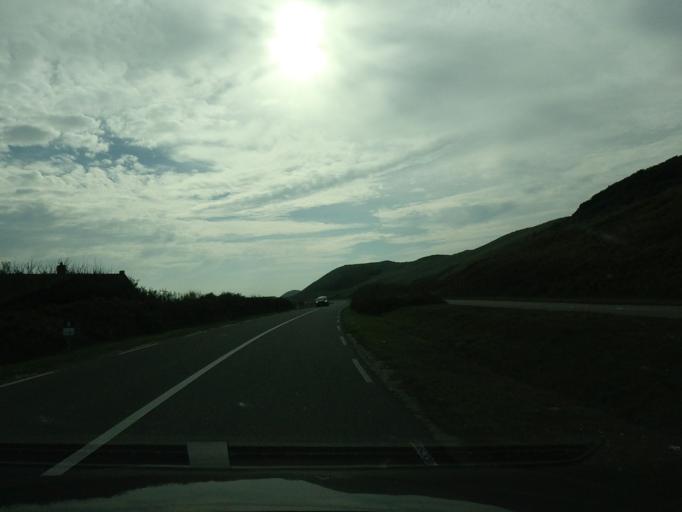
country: NL
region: North Holland
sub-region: Gemeente Schagen
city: Schagen
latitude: 52.8481
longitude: 4.6985
